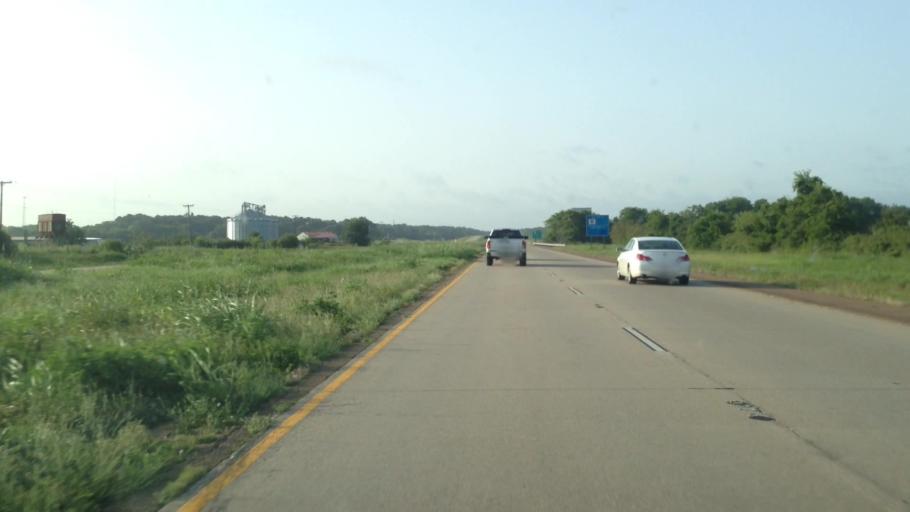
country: US
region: Louisiana
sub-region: Rapides Parish
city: Woodworth
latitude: 31.1742
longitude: -92.4653
